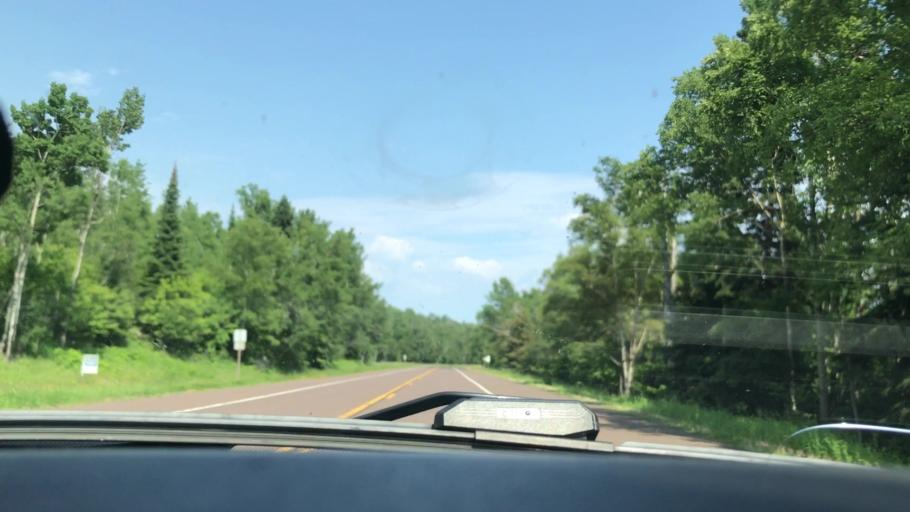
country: US
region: Minnesota
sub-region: Cook County
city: Grand Marais
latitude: 47.7773
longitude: -90.2213
